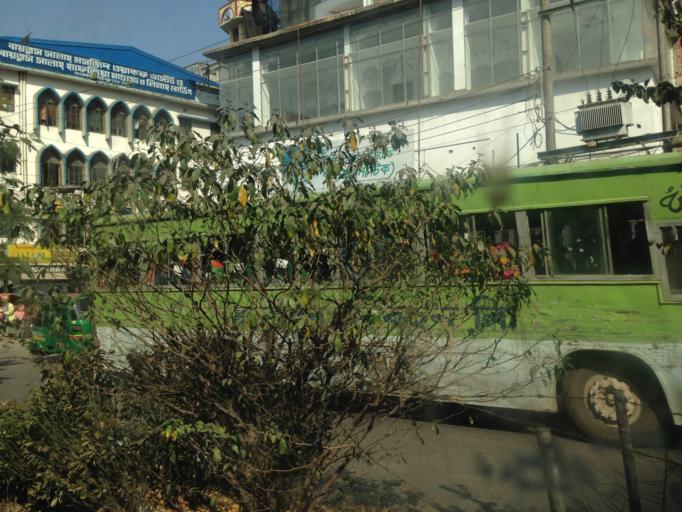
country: BD
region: Dhaka
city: Azimpur
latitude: 23.7473
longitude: 90.3805
